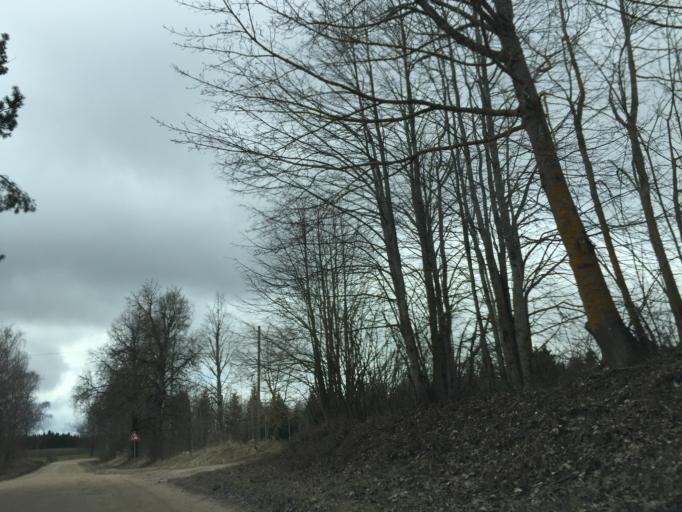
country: LV
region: Ilukste
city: Ilukste
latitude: 56.0656
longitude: 26.1118
